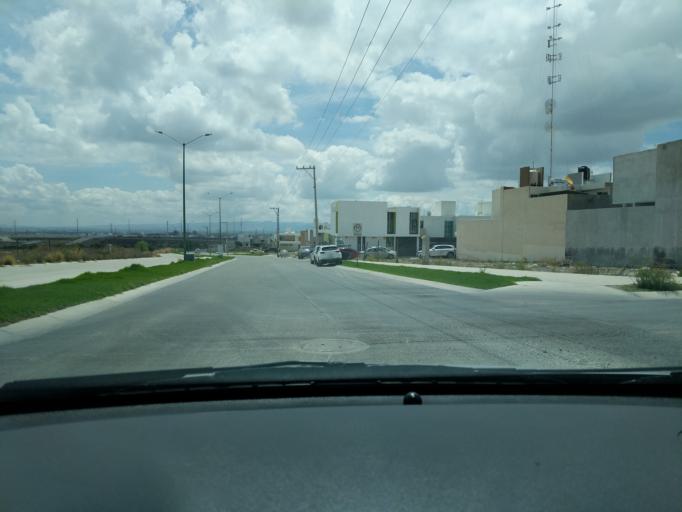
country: MX
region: San Luis Potosi
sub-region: Mexquitic de Carmona
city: Guadalupe Victoria
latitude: 22.1611
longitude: -101.0531
